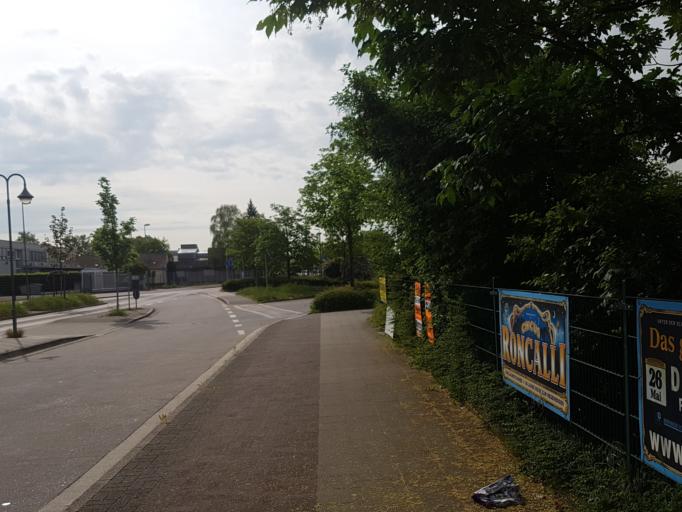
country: DE
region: North Rhine-Westphalia
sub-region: Regierungsbezirk Dusseldorf
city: Neuss
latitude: 51.1609
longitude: 6.7316
